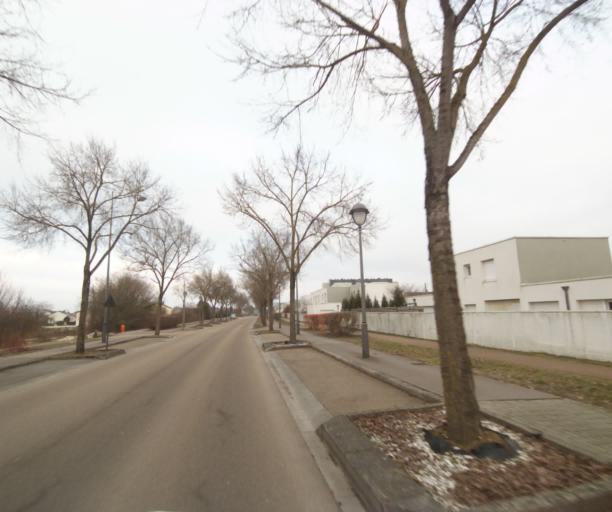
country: FR
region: Champagne-Ardenne
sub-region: Departement de la Haute-Marne
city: Bettancourt-la-Ferree
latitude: 48.6371
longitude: 4.9753
